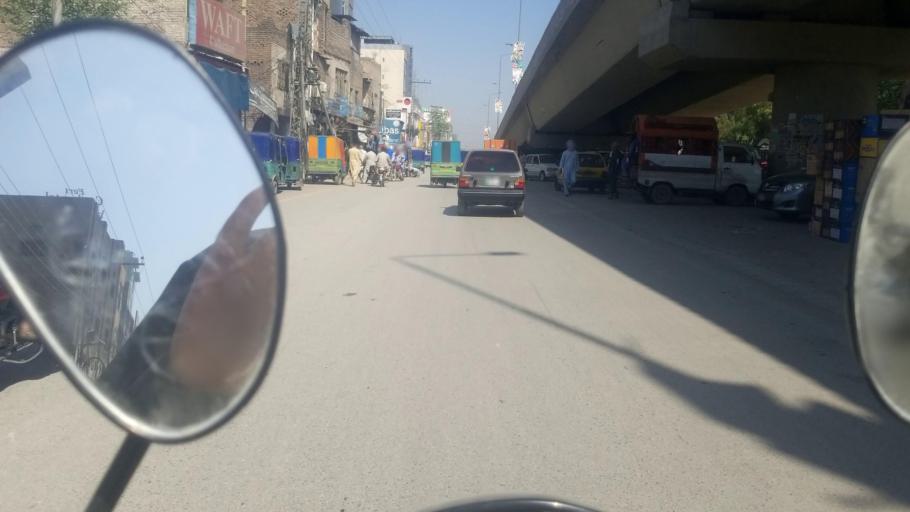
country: PK
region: Khyber Pakhtunkhwa
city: Peshawar
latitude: 34.0149
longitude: 71.5751
